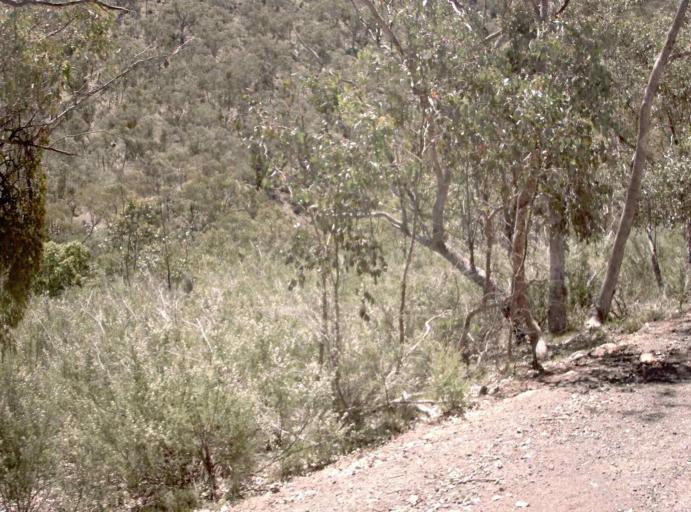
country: AU
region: New South Wales
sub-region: Snowy River
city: Jindabyne
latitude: -37.0768
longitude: 148.4616
